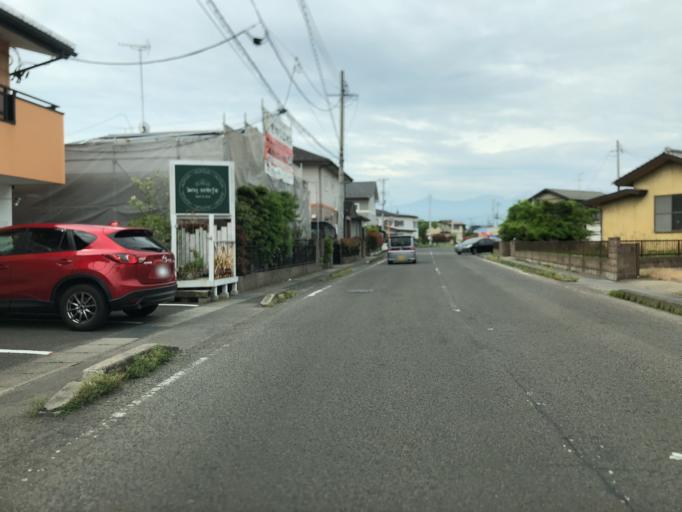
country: JP
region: Fukushima
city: Fukushima-shi
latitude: 37.7872
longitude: 140.4560
